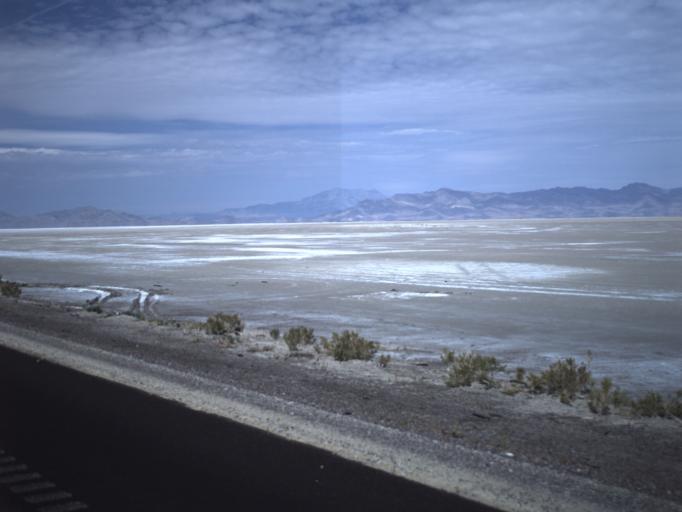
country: US
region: Utah
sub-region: Tooele County
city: Wendover
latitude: 40.7342
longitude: -113.6021
